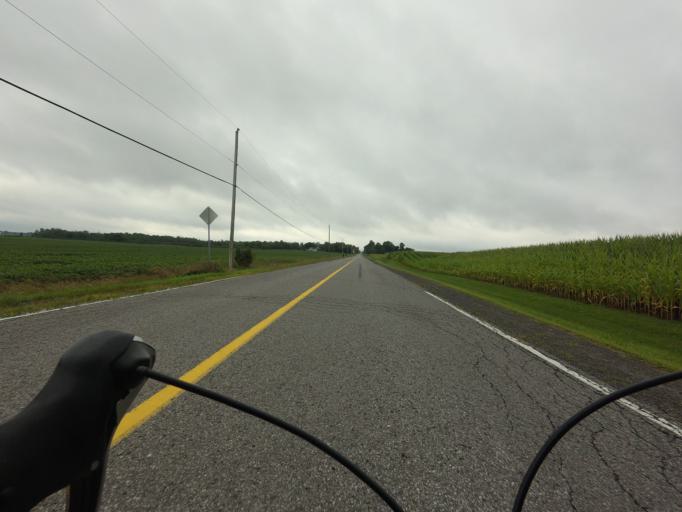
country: CA
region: Ontario
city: Bells Corners
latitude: 45.1115
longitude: -75.7812
